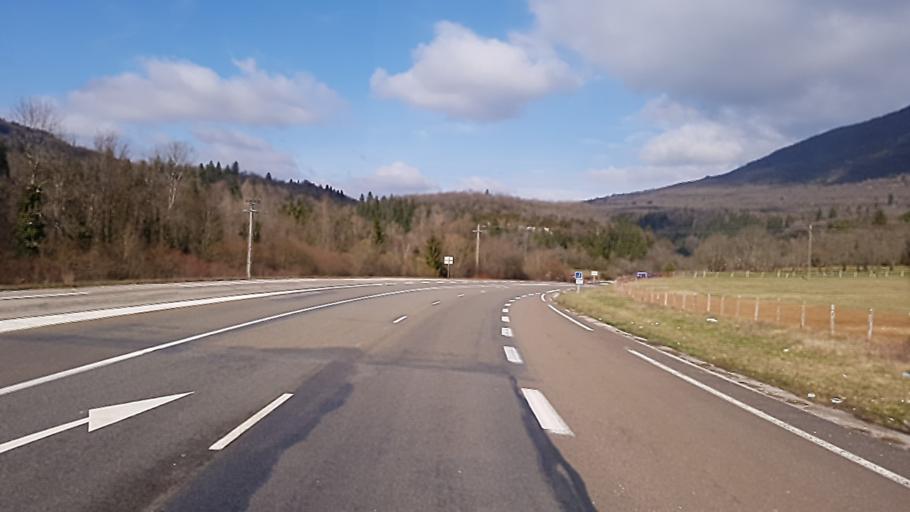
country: FR
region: Rhone-Alpes
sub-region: Departement de l'Ain
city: Dortan
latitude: 46.3335
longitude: 5.6807
